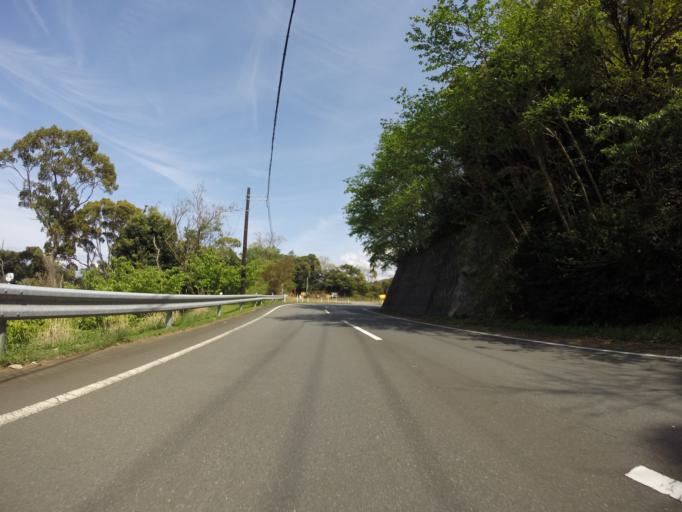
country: JP
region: Shizuoka
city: Heda
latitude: 35.0223
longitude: 138.7980
